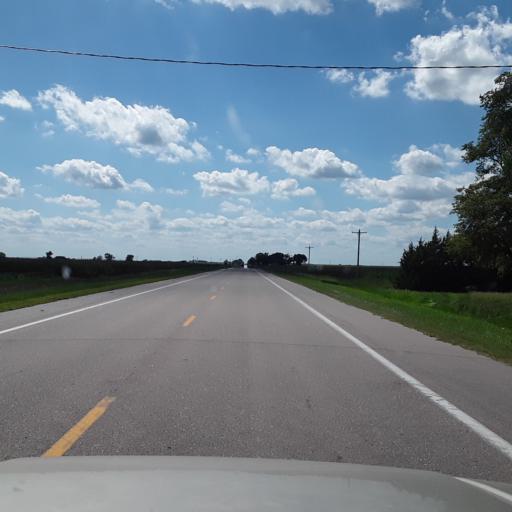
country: US
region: Nebraska
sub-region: Merrick County
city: Central City
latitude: 41.1910
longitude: -97.9914
